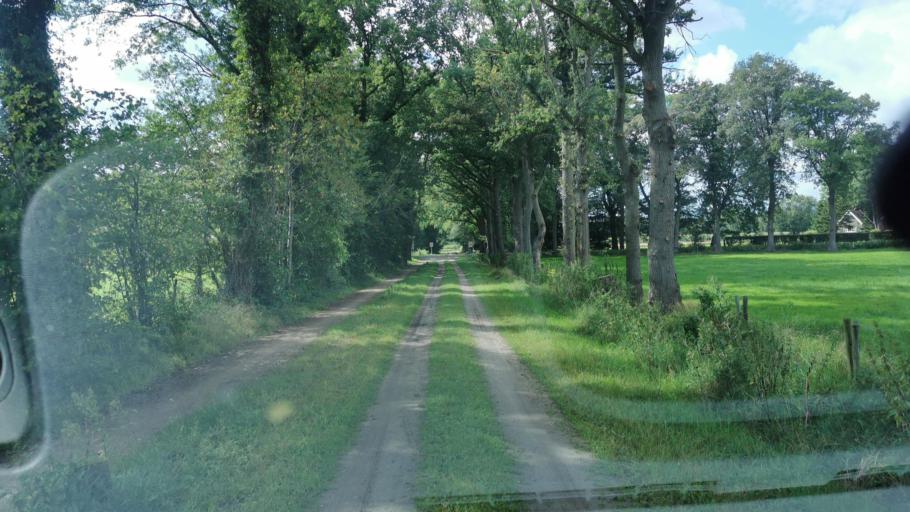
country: NL
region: Overijssel
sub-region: Gemeente Losser
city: Losser
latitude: 52.2555
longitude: 6.9913
